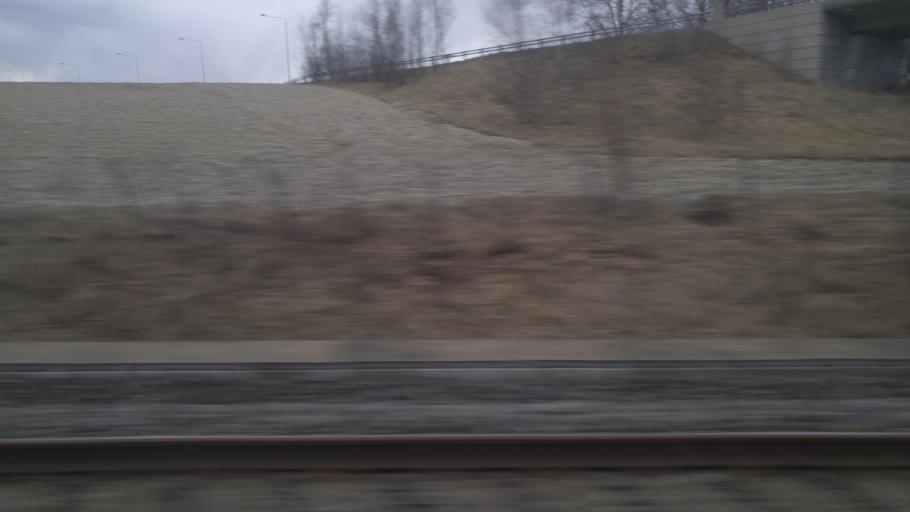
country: NO
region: Akershus
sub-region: Ullensaker
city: Jessheim
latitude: 60.1277
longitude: 11.1596
